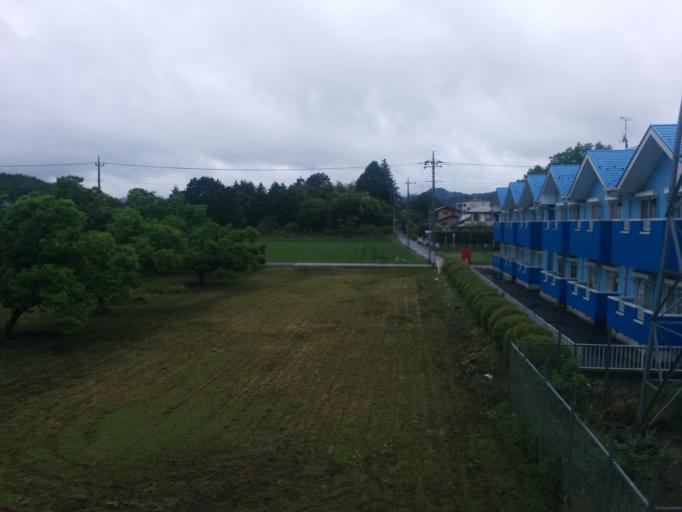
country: JP
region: Tochigi
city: Imaichi
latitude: 36.6830
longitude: 139.7335
